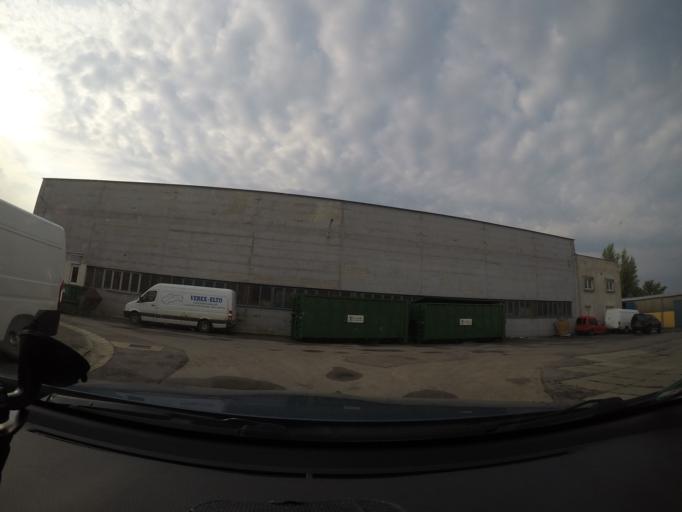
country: SK
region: Trenciansky
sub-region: Okres Trencin
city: Trencin
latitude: 48.8921
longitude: 18.0211
